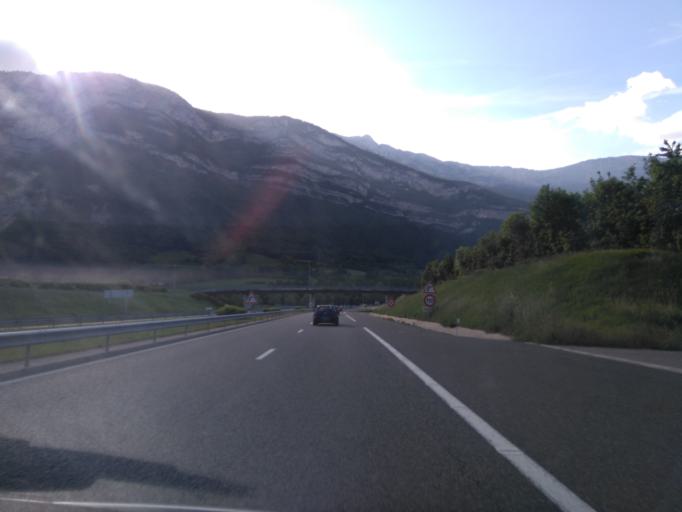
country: FR
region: Rhone-Alpes
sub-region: Departement de l'Isere
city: Allieres-et-Risset
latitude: 45.0858
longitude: 5.6731
